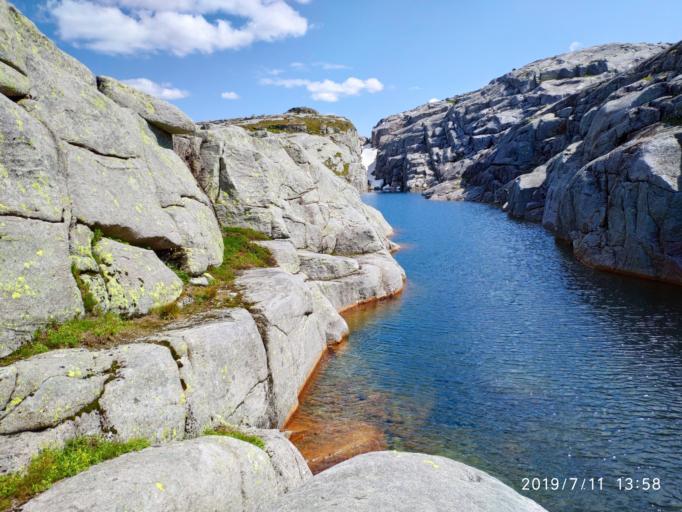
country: NO
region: Vest-Agder
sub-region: Sirdal
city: Tonstad
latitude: 59.0329
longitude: 6.5959
